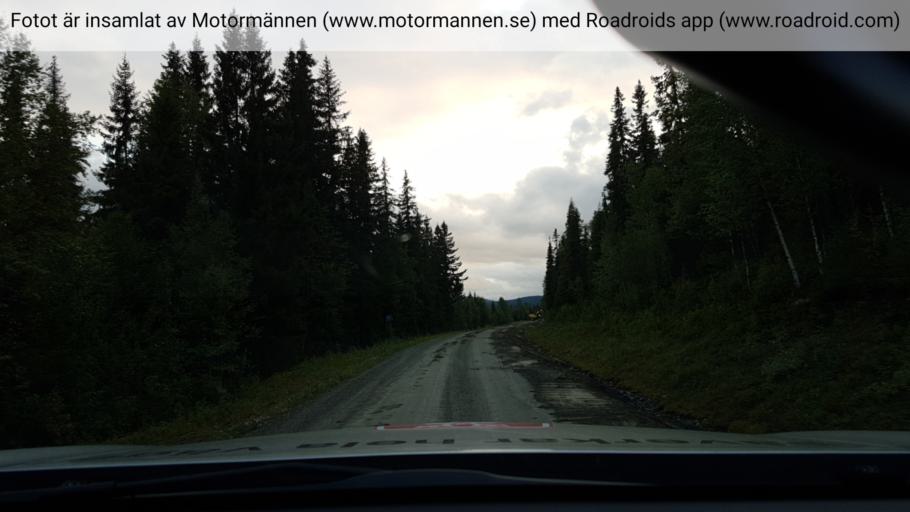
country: SE
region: Vaesterbotten
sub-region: Vilhelmina Kommun
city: Sjoberg
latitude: 65.4973
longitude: 15.5339
